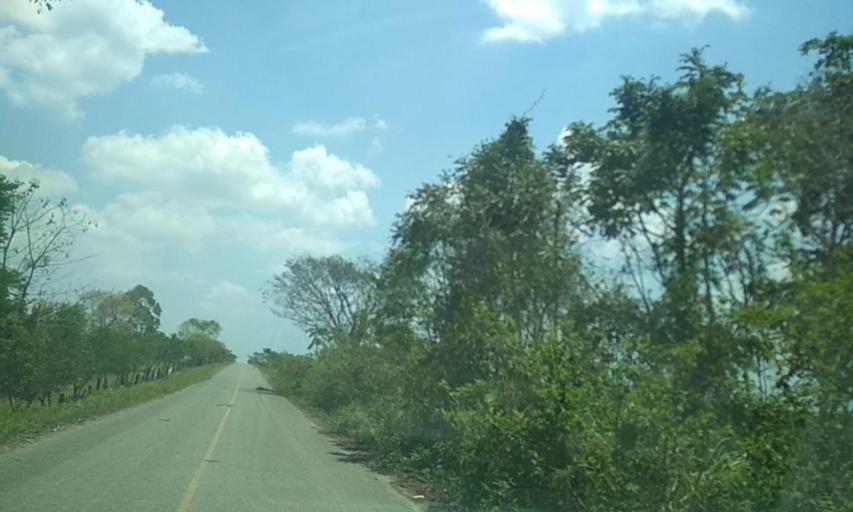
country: MX
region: Tabasco
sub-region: Huimanguillo
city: Francisco Rueda
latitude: 17.8192
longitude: -93.8709
